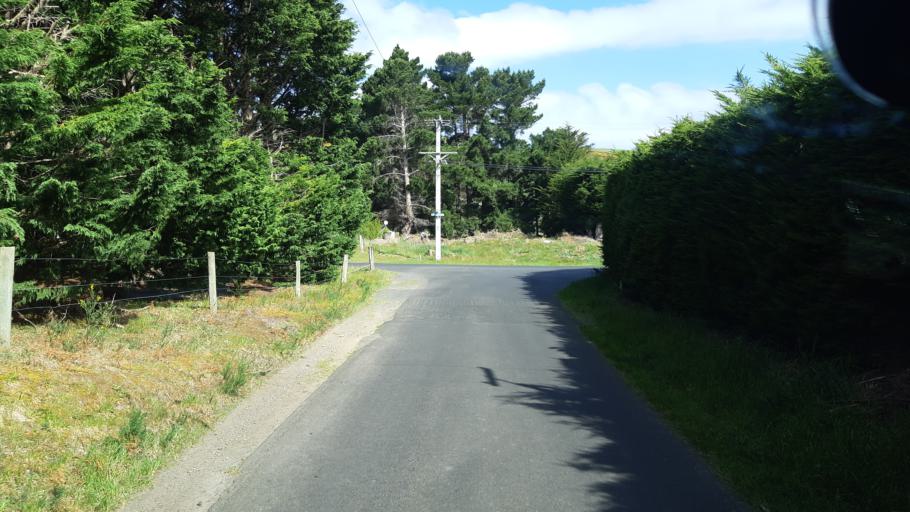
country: NZ
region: Otago
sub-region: Dunedin City
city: Portobello
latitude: -45.8155
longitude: 170.6727
